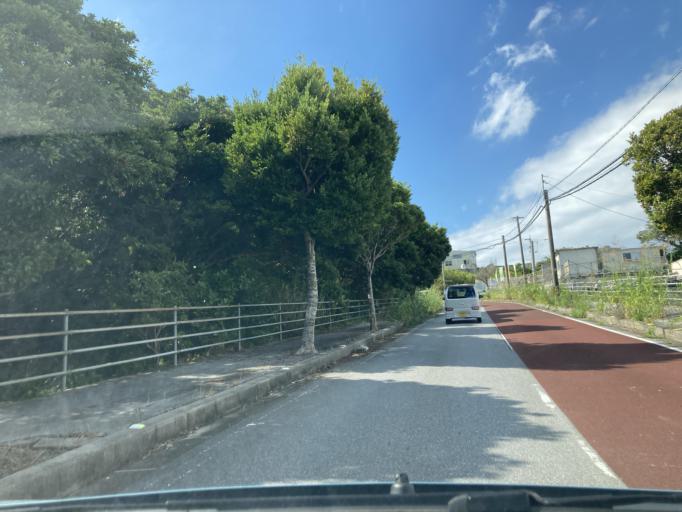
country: JP
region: Okinawa
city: Ginowan
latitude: 26.2459
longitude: 127.7571
